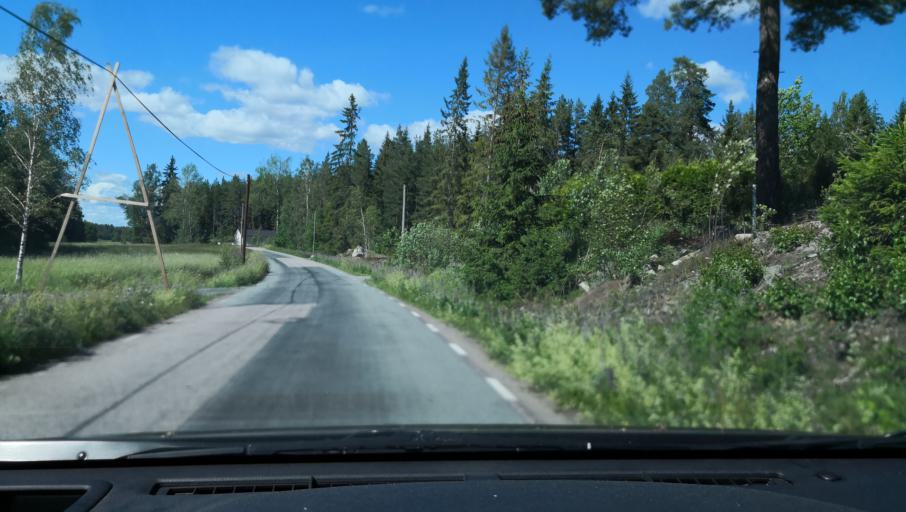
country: SE
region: Soedermanland
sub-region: Eskilstuna Kommun
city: Hallbybrunn
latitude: 59.3150
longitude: 16.3786
